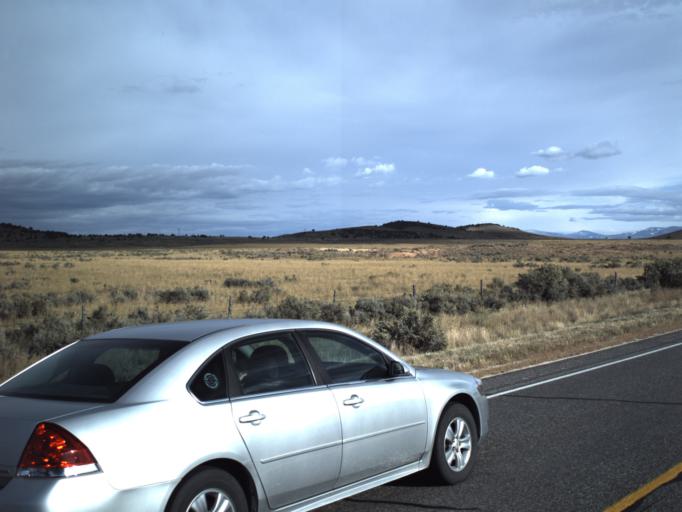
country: US
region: Utah
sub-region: Sevier County
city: Aurora
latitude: 39.0239
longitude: -112.0359
